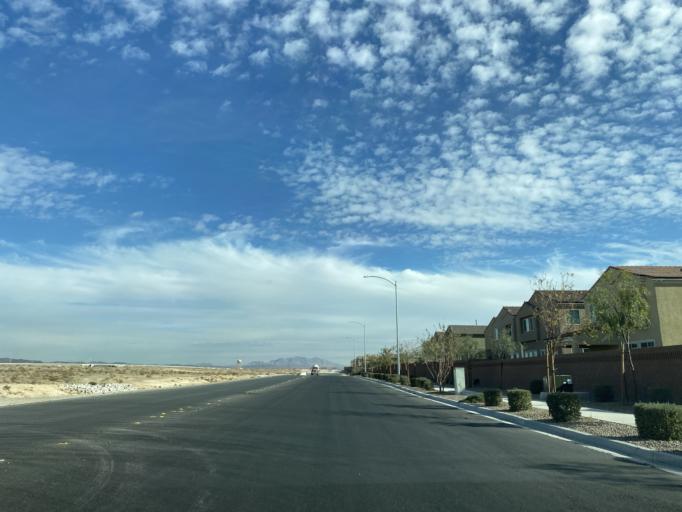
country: US
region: Nevada
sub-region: Clark County
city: Nellis Air Force Base
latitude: 36.2767
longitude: -115.0748
